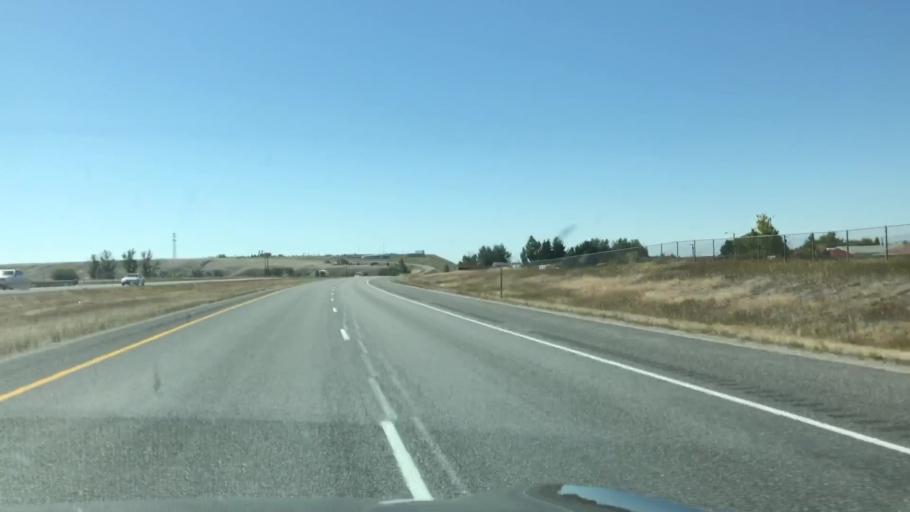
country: US
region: Montana
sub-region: Powell County
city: Deer Lodge
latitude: 46.3948
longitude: -112.7185
